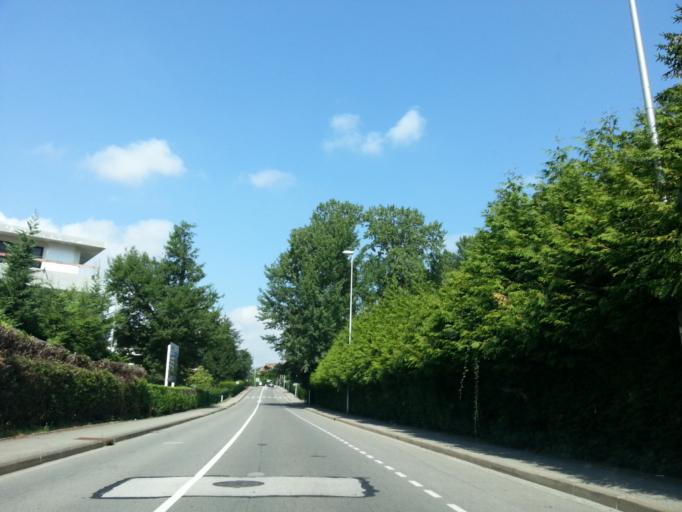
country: FR
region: Rhone-Alpes
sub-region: Departement de la Haute-Savoie
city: Annecy-le-Vieux
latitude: 45.9135
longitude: 6.1539
